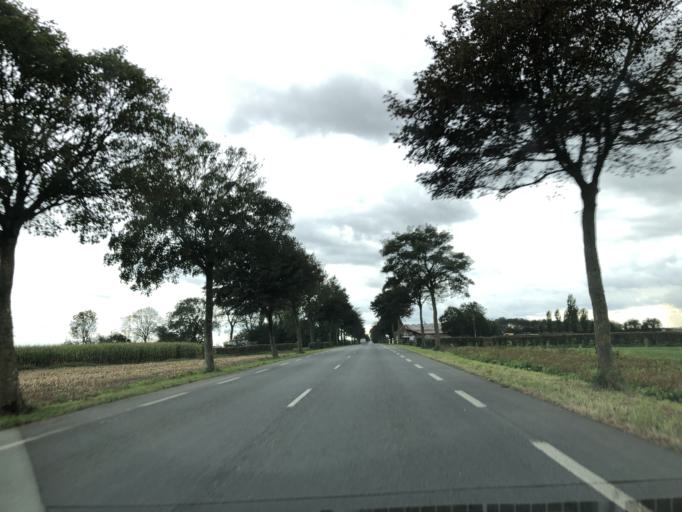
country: FR
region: Nord-Pas-de-Calais
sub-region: Departement du Pas-de-Calais
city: Auchy-les-Hesdin
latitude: 50.4618
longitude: 2.0991
